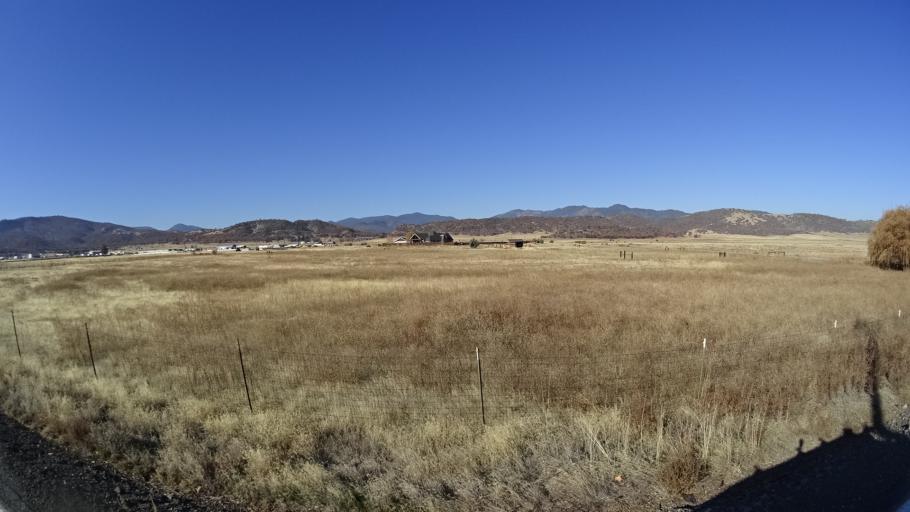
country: US
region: California
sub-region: Siskiyou County
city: Yreka
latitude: 41.7141
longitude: -122.5935
